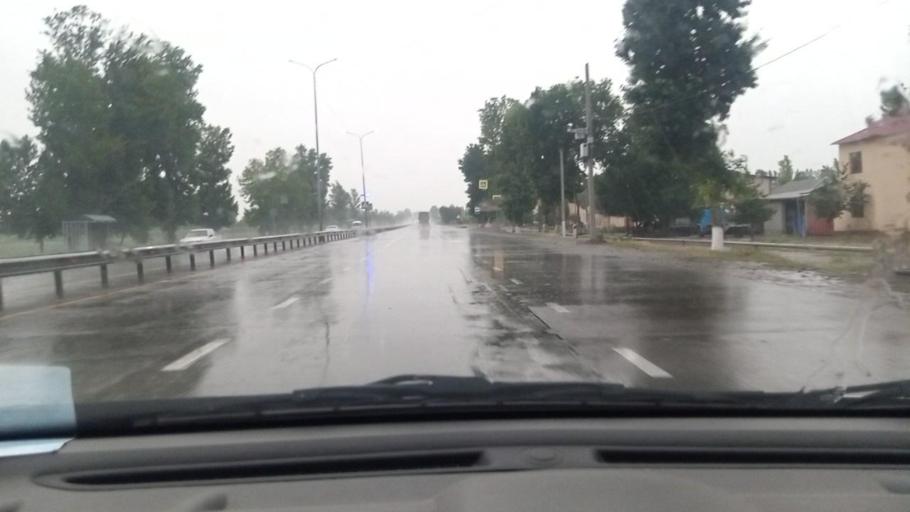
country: UZ
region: Toshkent Shahri
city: Bektemir
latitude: 41.1552
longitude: 69.4242
